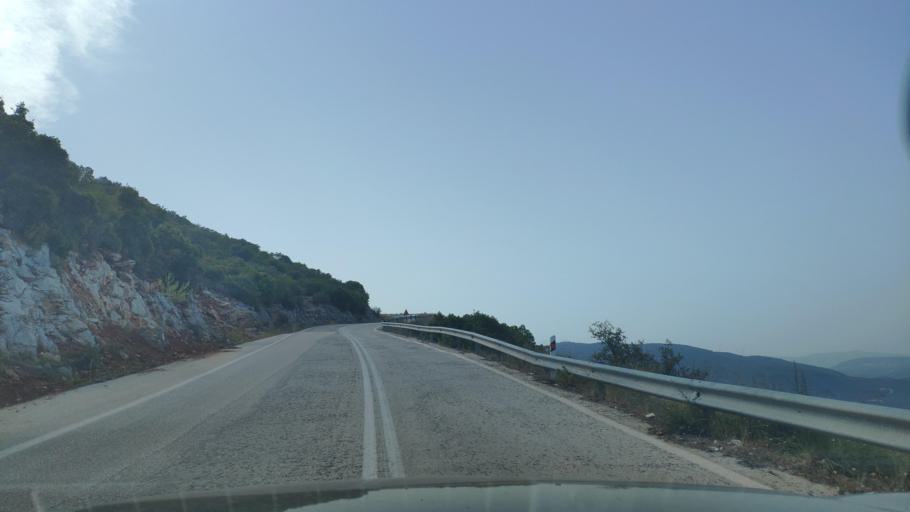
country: GR
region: Peloponnese
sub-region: Nomos Argolidos
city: Palaia Epidavros
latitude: 37.6026
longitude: 23.1593
